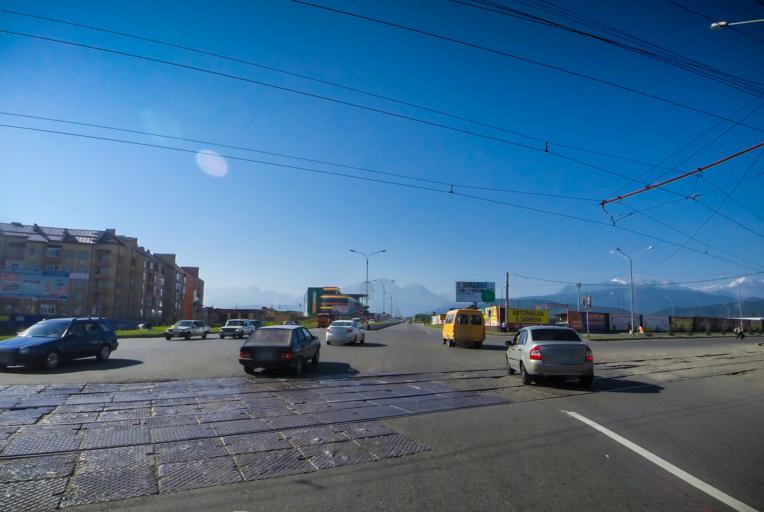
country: RU
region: North Ossetia
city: Vladikavkaz
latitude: 43.0365
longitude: 44.6411
